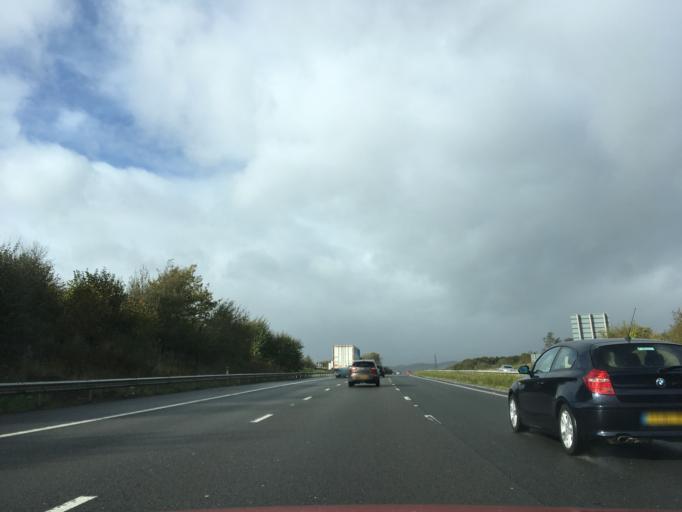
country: GB
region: Wales
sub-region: Caerphilly County Borough
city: Machen
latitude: 51.5416
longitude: -3.1292
